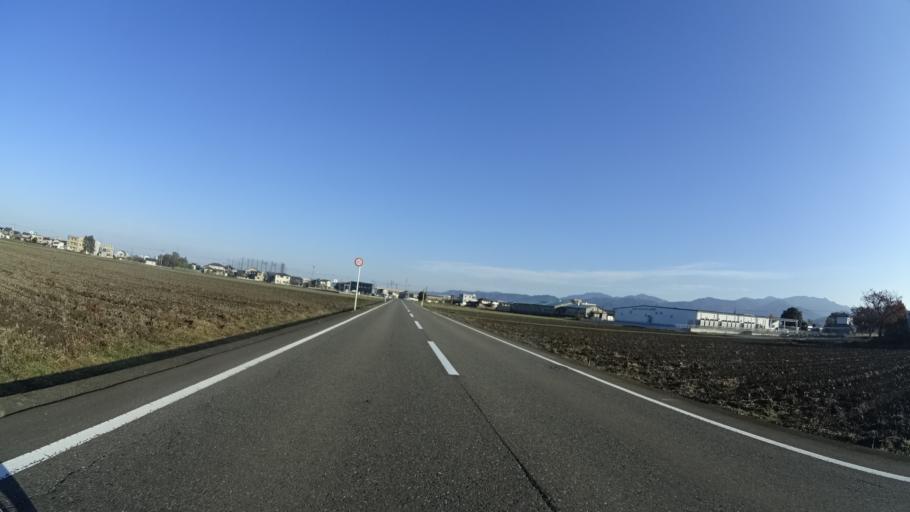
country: JP
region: Fukui
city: Fukui-shi
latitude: 36.0778
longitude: 136.2585
